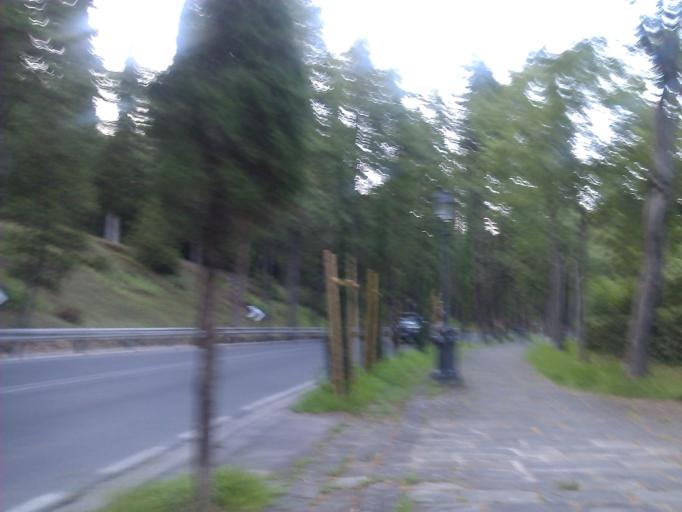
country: IT
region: Tuscany
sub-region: Province of Florence
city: Florence
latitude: 43.7573
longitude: 11.2682
